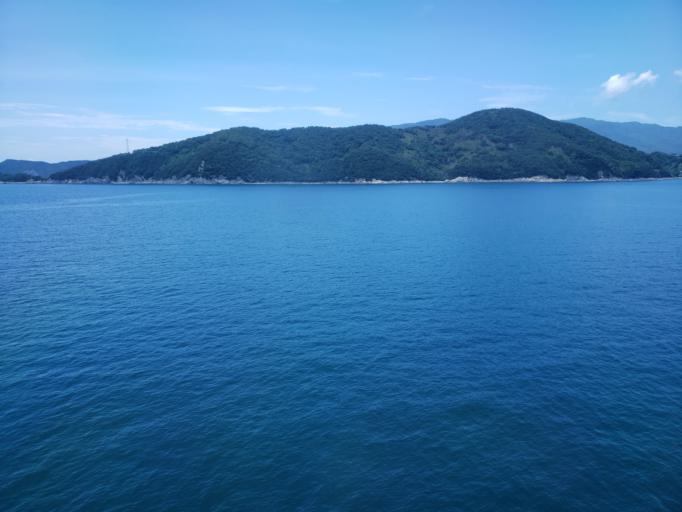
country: JP
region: Kagawa
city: Tonosho
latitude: 34.4410
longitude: 134.3013
